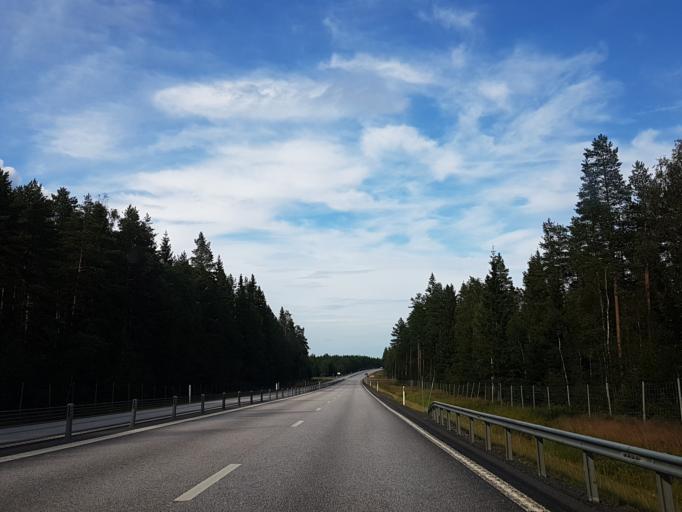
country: SE
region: Vaesterbotten
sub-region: Umea Kommun
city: Saevar
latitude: 63.9793
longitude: 20.7248
